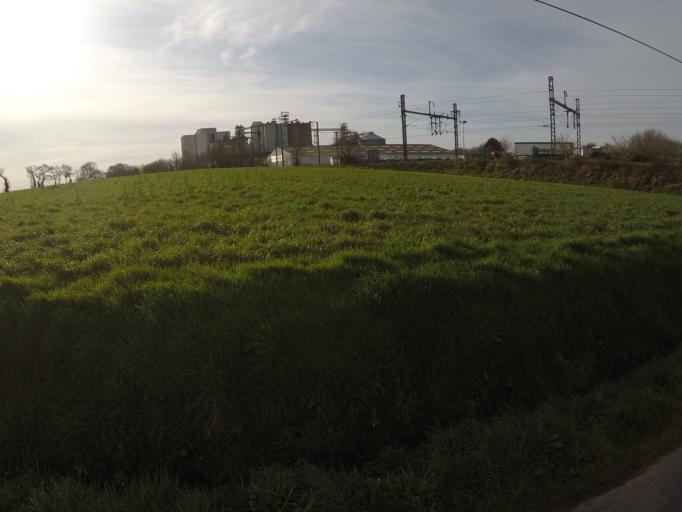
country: FR
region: Brittany
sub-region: Departement des Cotes-d'Armor
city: Plouagat
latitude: 48.5335
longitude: -2.9696
